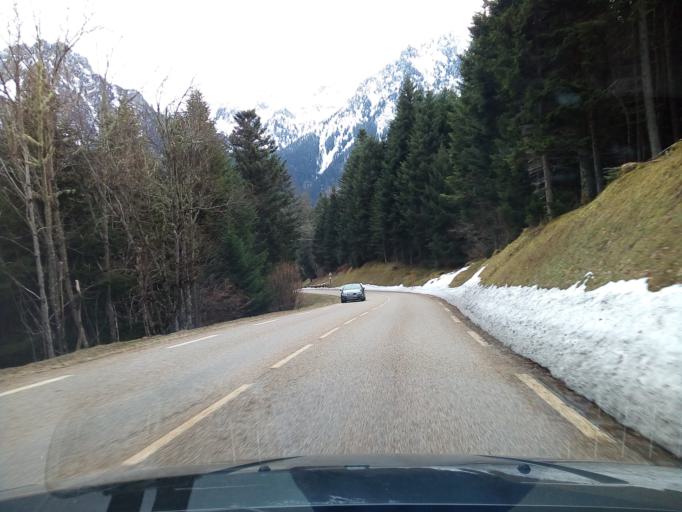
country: FR
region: Rhone-Alpes
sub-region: Departement de l'Isere
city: Revel
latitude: 45.1520
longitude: 5.8839
